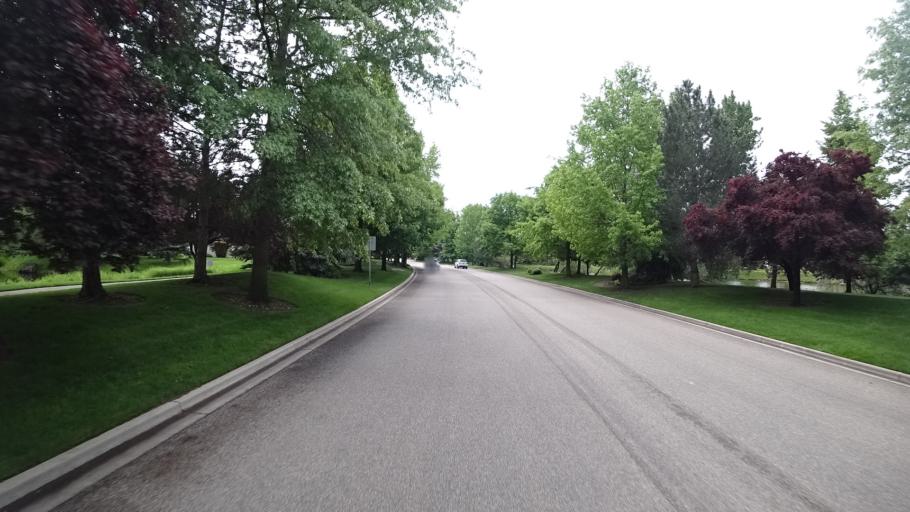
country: US
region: Idaho
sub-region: Ada County
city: Eagle
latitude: 43.6806
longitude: -116.3482
